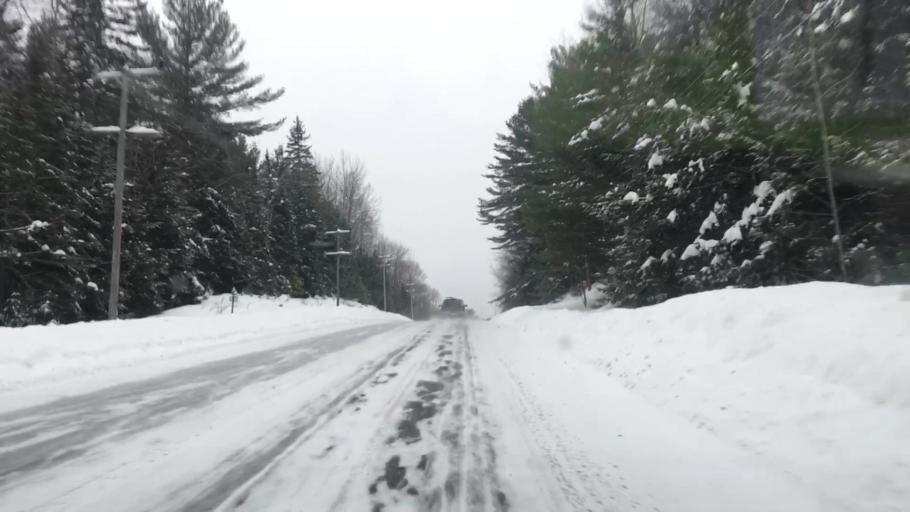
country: US
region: Maine
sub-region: Penobscot County
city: Medway
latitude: 45.5976
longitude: -68.4742
